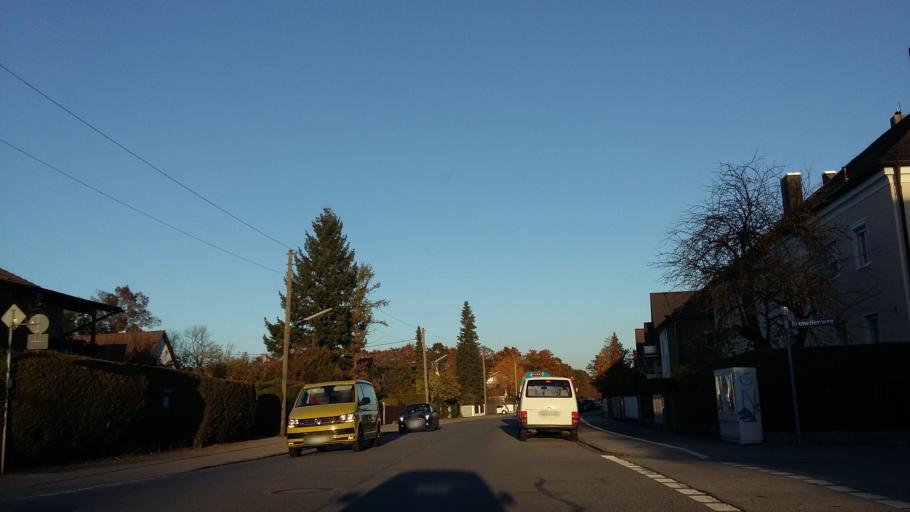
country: DE
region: Bavaria
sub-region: Upper Bavaria
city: Pasing
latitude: 48.1284
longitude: 11.4756
